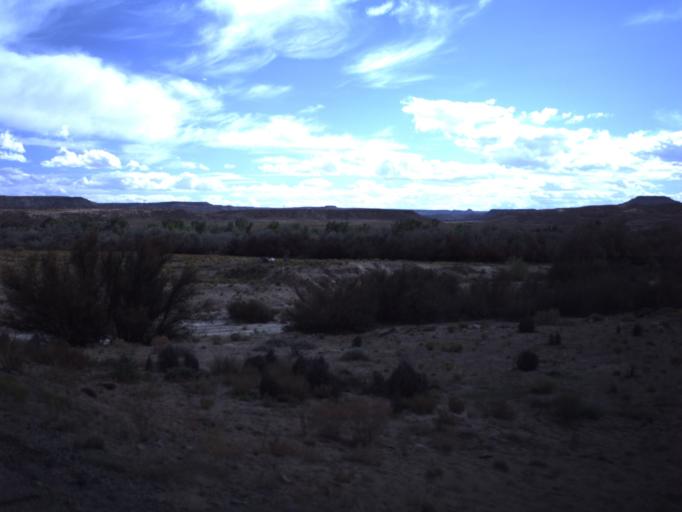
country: US
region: Utah
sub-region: San Juan County
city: Blanding
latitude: 37.2499
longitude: -109.2560
